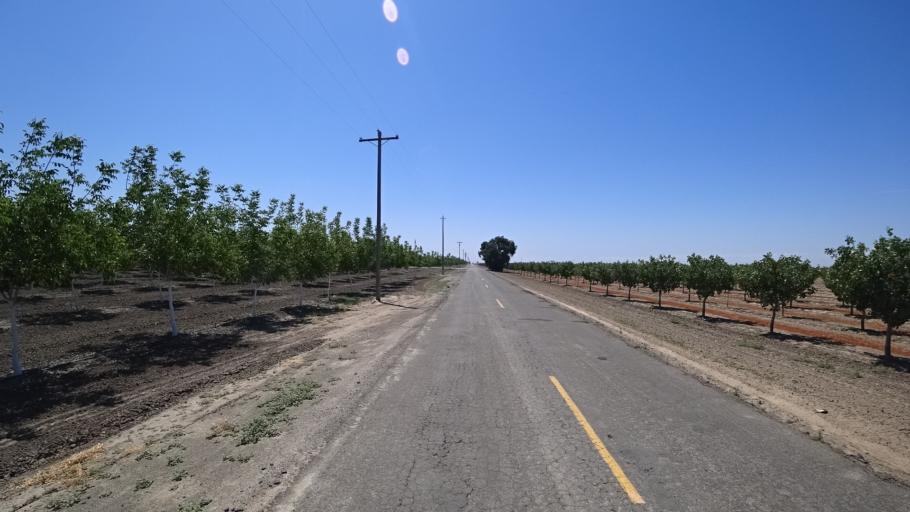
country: US
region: California
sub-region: Kings County
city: Armona
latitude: 36.2466
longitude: -119.7268
